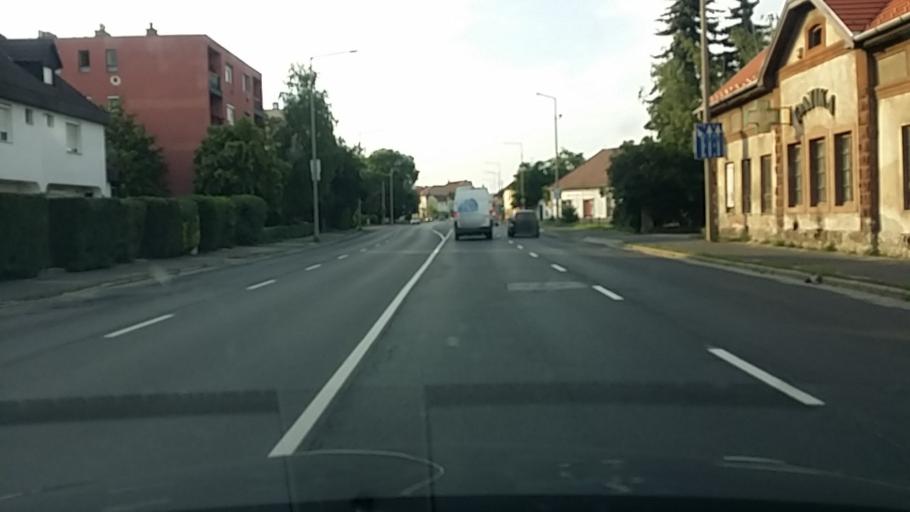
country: HU
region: Borsod-Abauj-Zemplen
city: Miskolc
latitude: 48.0707
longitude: 20.7902
